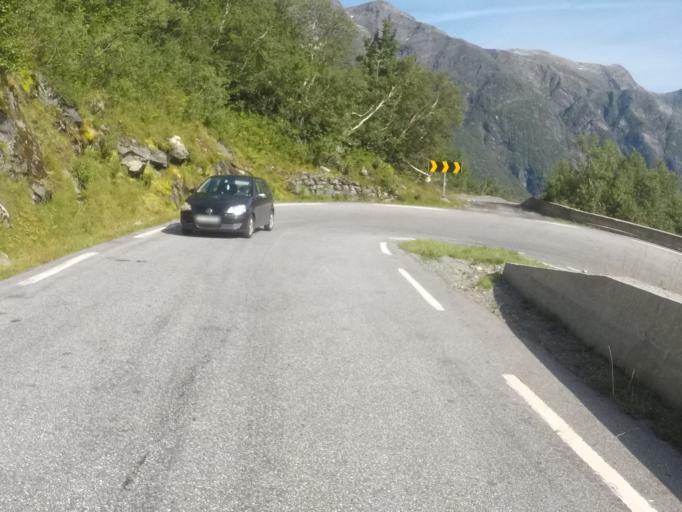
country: NO
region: Sogn og Fjordane
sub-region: Balestrand
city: Balestrand
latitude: 61.3574
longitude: 6.5230
